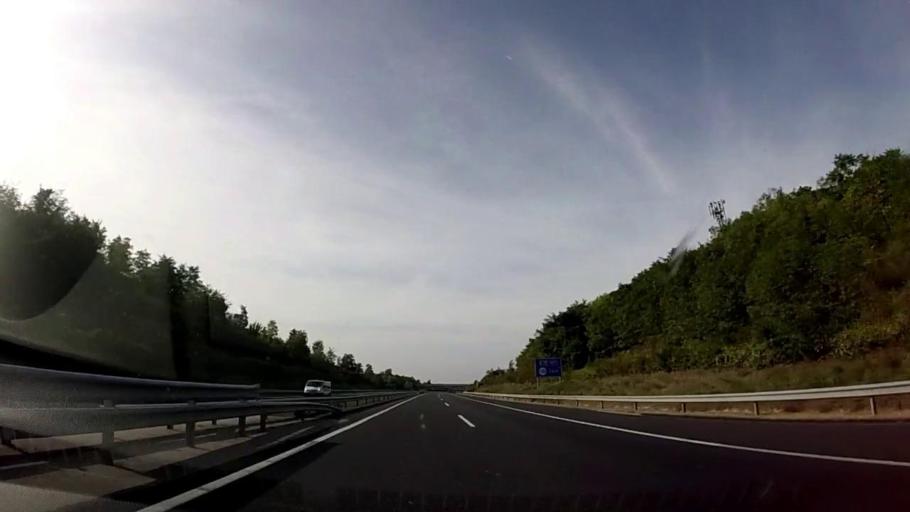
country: HU
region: Somogy
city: Balatonszarszo
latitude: 46.8152
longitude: 17.8503
